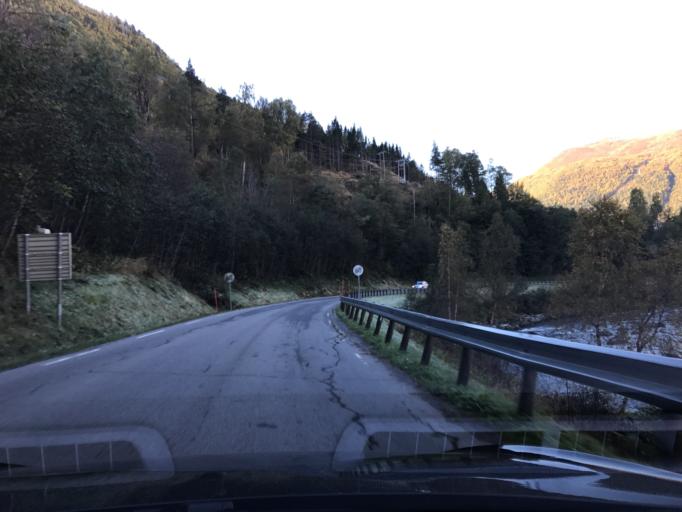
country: NO
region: More og Romsdal
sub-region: Norddal
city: Valldal
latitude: 62.3126
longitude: 7.2903
